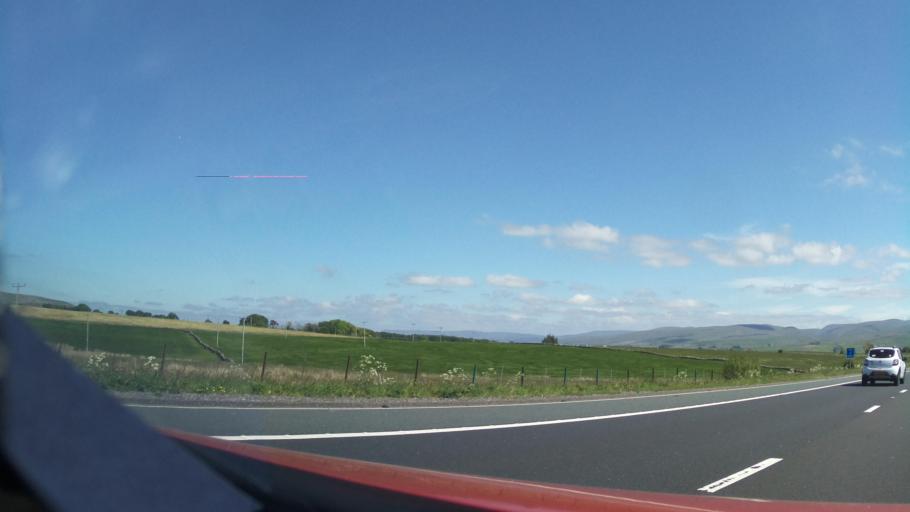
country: GB
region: England
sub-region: Cumbria
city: Sedbergh
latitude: 54.4608
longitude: -2.6162
